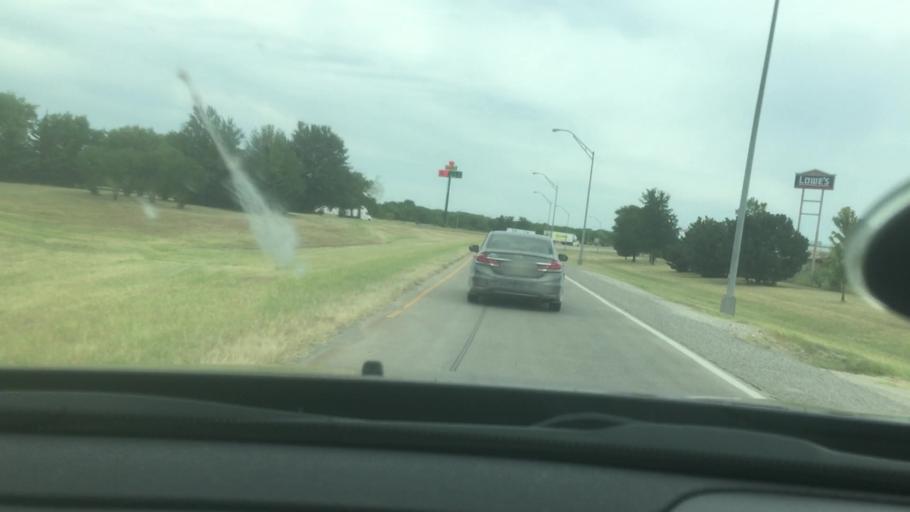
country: US
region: Oklahoma
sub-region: Carter County
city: Ardmore
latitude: 34.1884
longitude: -97.1639
